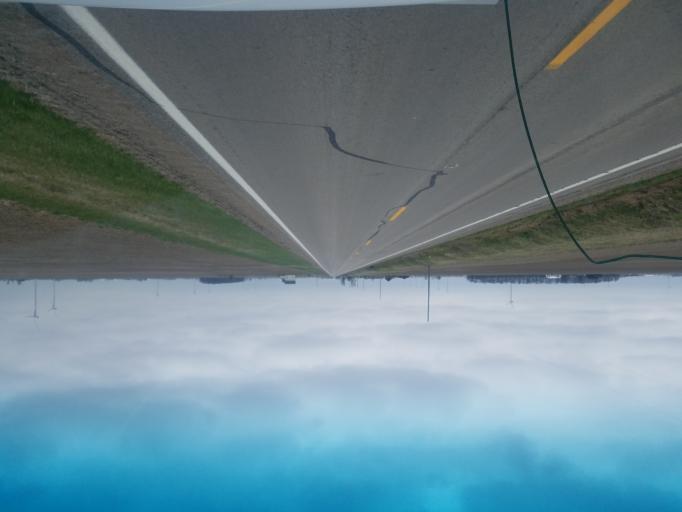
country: US
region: Ohio
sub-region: Van Wert County
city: Convoy
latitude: 40.9825
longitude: -84.7264
